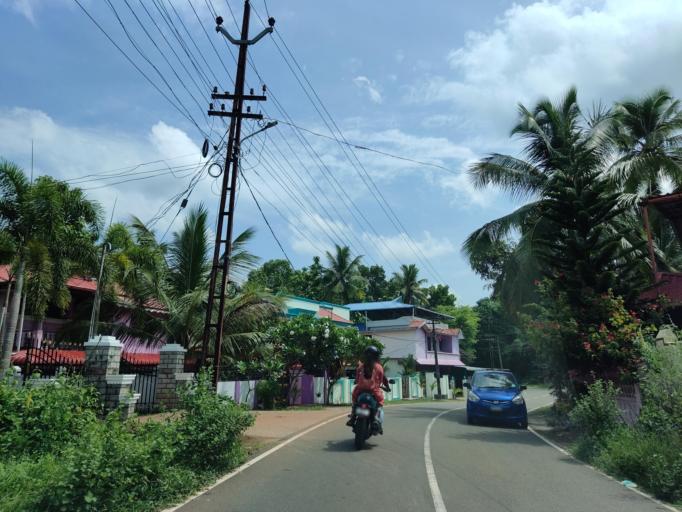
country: IN
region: Kerala
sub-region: Alappuzha
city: Mavelikara
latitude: 9.2748
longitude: 76.5662
